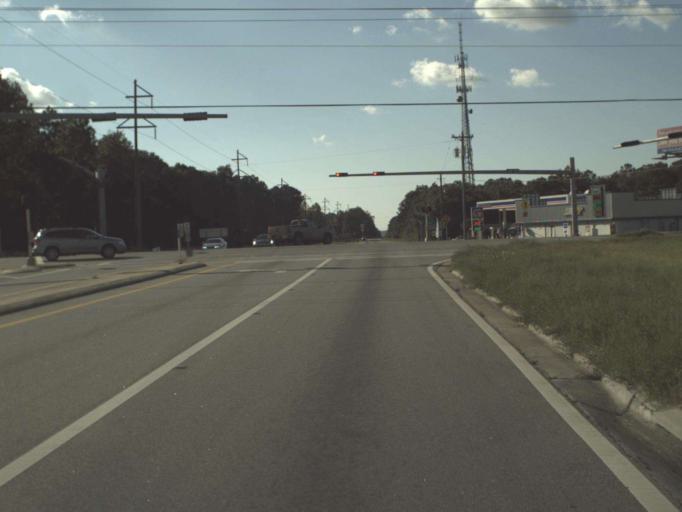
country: US
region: Florida
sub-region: Bay County
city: Laguna Beach
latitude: 30.4427
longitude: -85.8734
